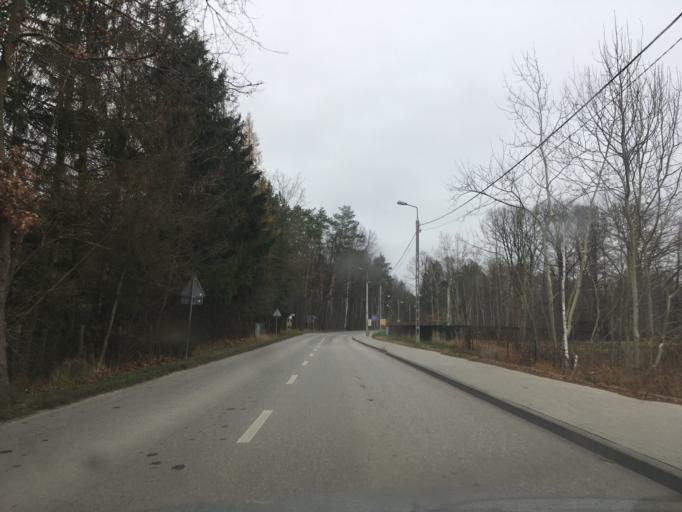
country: PL
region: Masovian Voivodeship
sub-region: Powiat piaseczynski
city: Lesznowola
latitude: 52.0766
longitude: 20.9366
